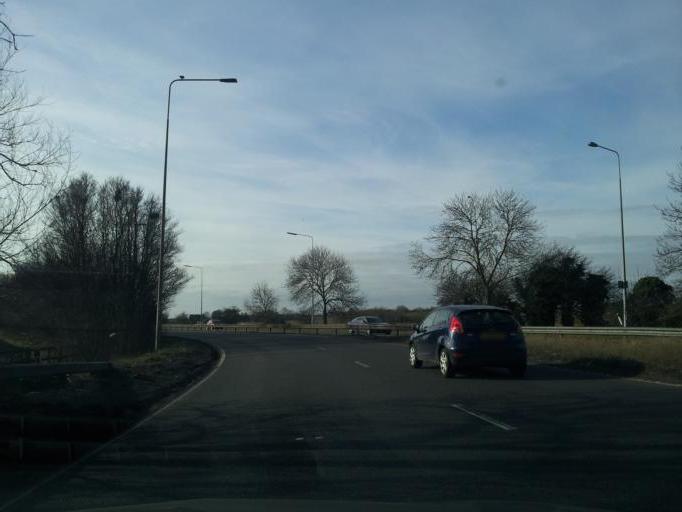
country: GB
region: England
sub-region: Central Bedfordshire
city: Biggleswade
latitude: 52.0920
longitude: -0.2738
